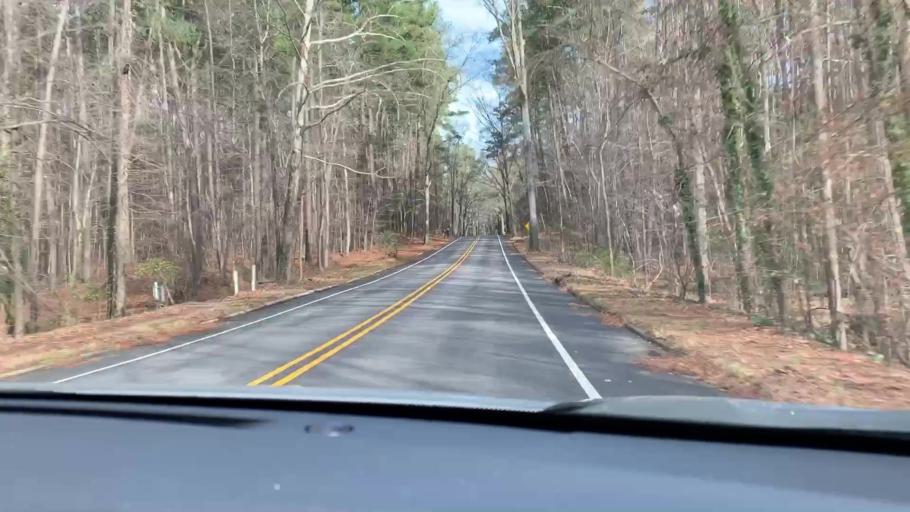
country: US
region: North Carolina
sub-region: Durham County
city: Durham
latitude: 35.9868
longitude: -78.9409
